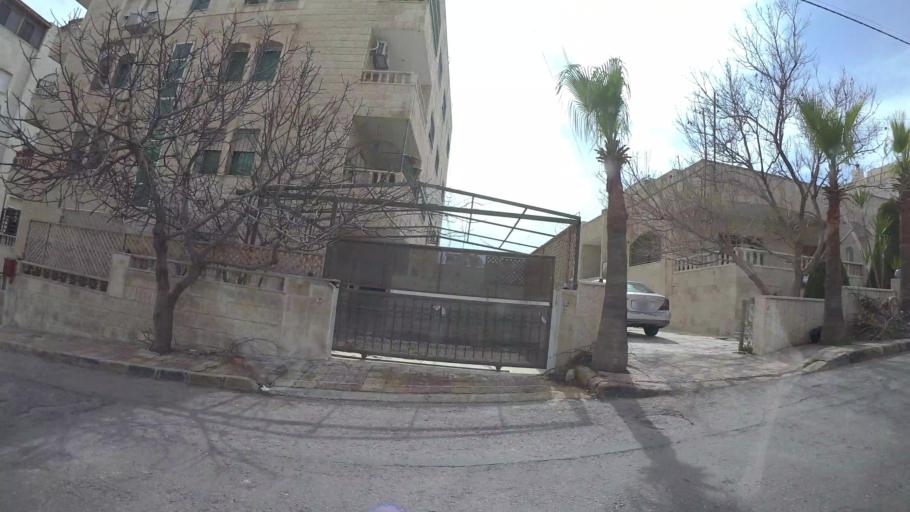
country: JO
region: Amman
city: Amman
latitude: 31.9974
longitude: 35.9368
